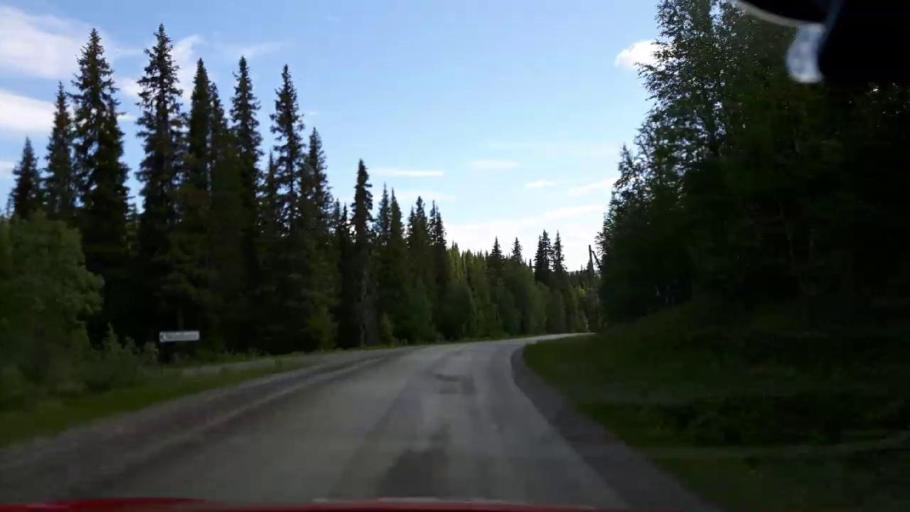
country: SE
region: Jaemtland
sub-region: Krokoms Kommun
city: Valla
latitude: 63.7845
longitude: 14.0489
